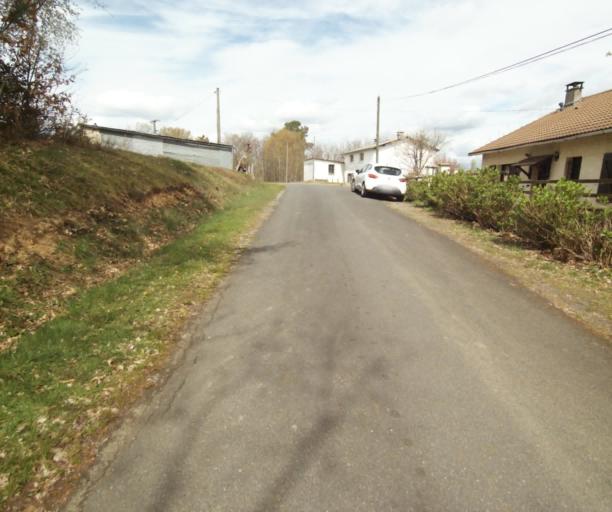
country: FR
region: Limousin
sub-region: Departement de la Correze
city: Sainte-Fortunade
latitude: 45.2014
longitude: 1.8453
